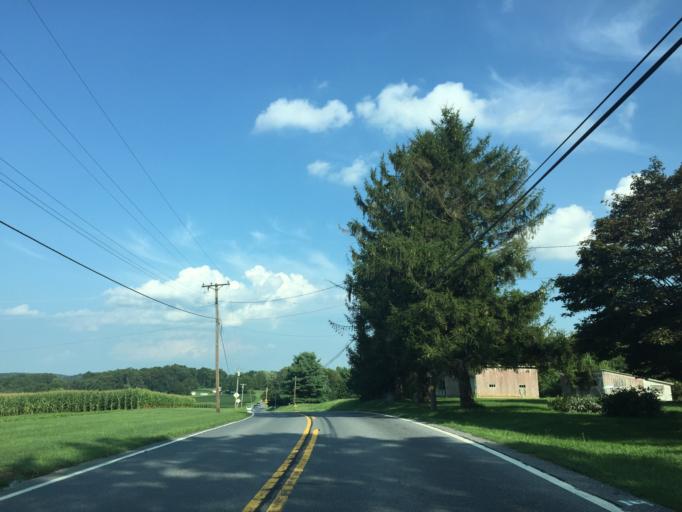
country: US
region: Maryland
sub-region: Carroll County
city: Hampstead
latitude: 39.5998
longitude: -76.7697
